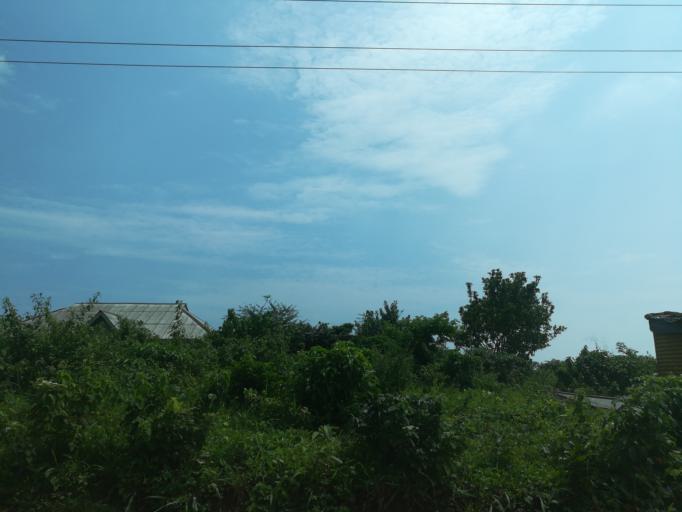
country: NG
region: Lagos
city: Ikorodu
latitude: 6.5929
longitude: 3.6408
